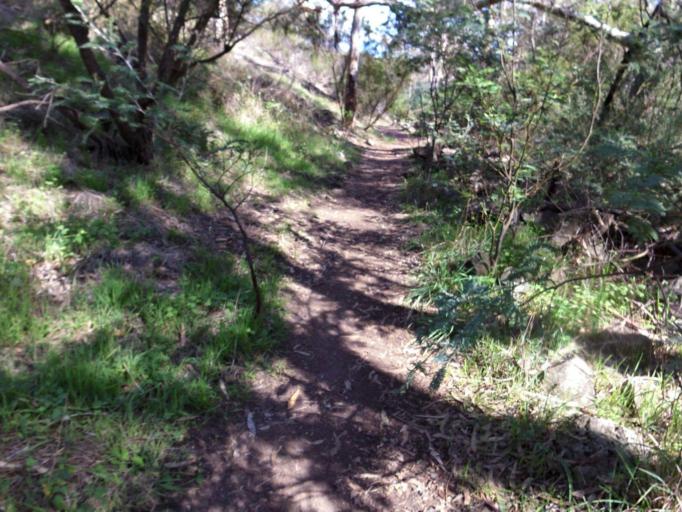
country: AU
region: Victoria
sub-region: Greater Geelong
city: Wandana Heights
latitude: -38.1494
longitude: 144.3099
